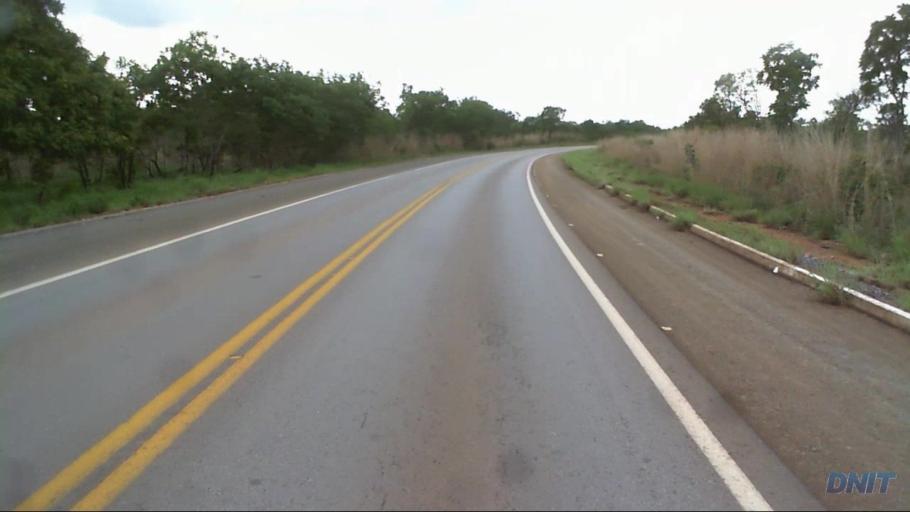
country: BR
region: Goias
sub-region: Barro Alto
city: Barro Alto
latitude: -14.7794
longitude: -49.0552
